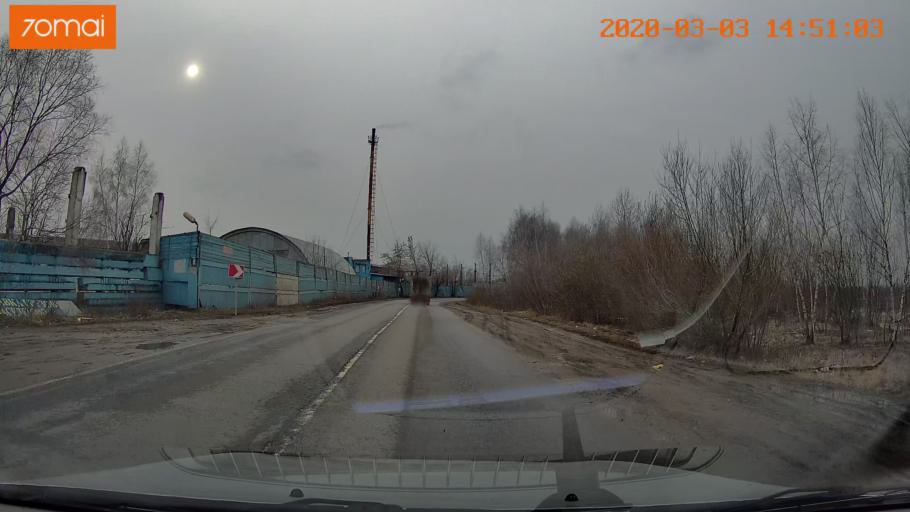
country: RU
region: Moskovskaya
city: Malakhovka
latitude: 55.6664
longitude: 38.0345
